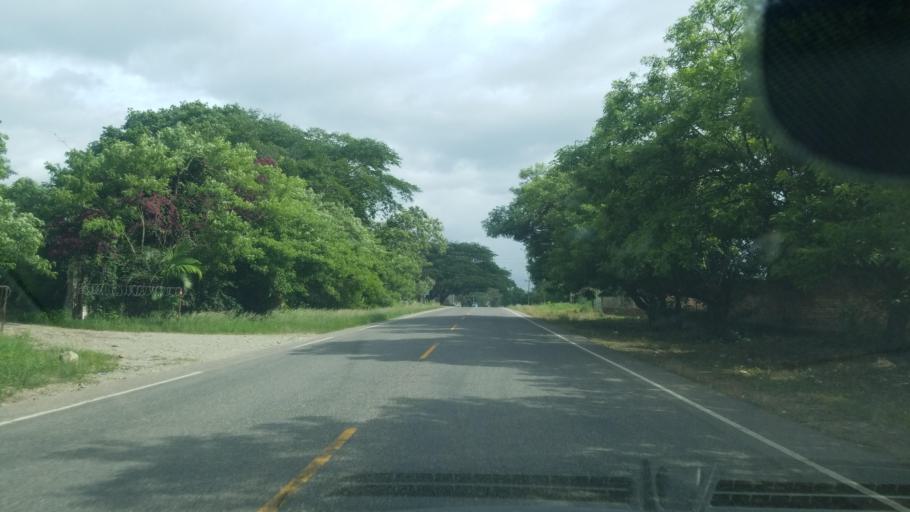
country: HN
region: Ocotepeque
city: Antigua Ocotepeque
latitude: 14.4053
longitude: -89.1956
